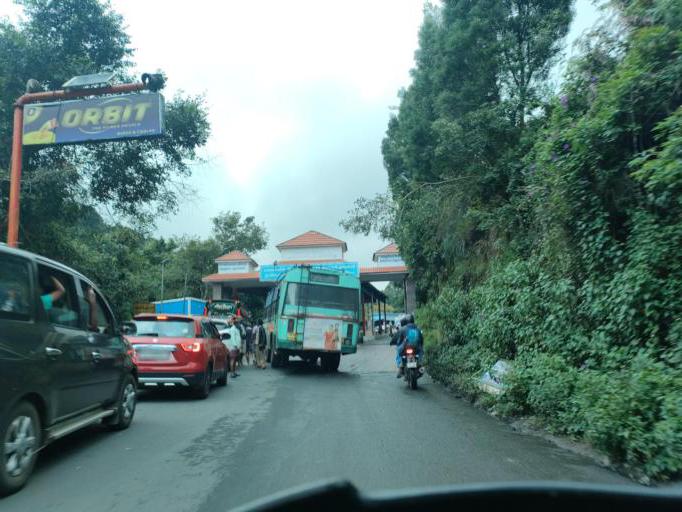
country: IN
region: Tamil Nadu
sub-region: Dindigul
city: Kodaikanal
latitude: 10.2421
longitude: 77.5123
